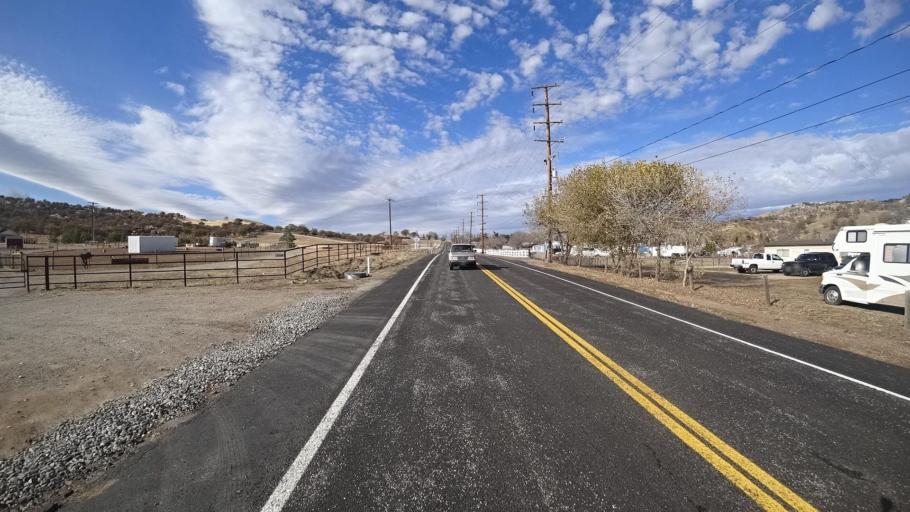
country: US
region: California
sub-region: Kern County
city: Golden Hills
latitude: 35.1094
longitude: -118.5146
